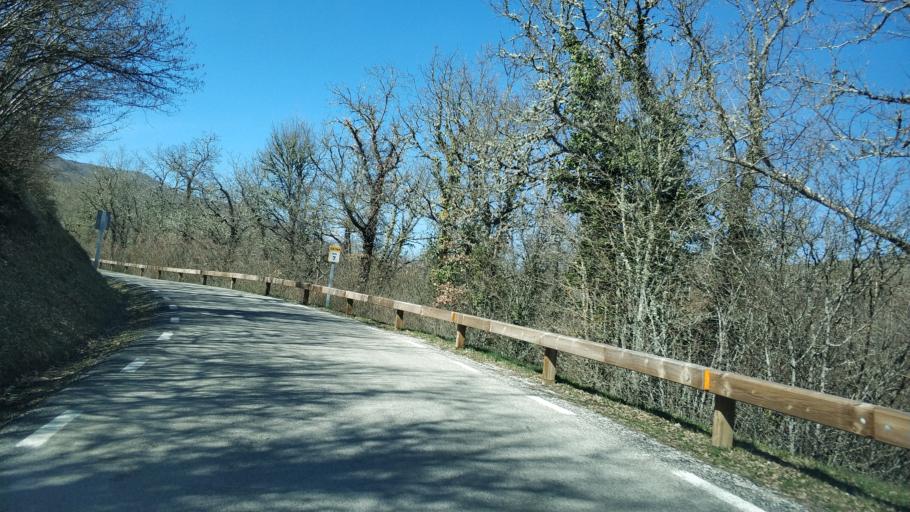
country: ES
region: Cantabria
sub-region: Provincia de Cantabria
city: Mataporquera
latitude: 42.8703
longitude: -4.0740
